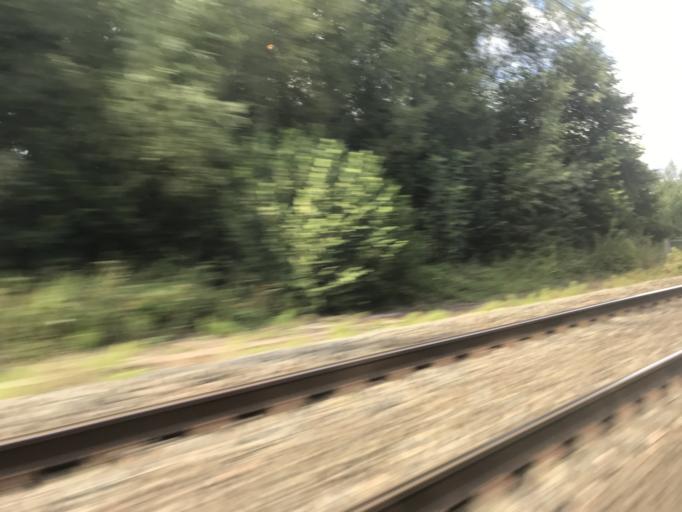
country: FR
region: Champagne-Ardenne
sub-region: Departement des Ardennes
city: Bazeilles
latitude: 49.6728
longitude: 5.0085
